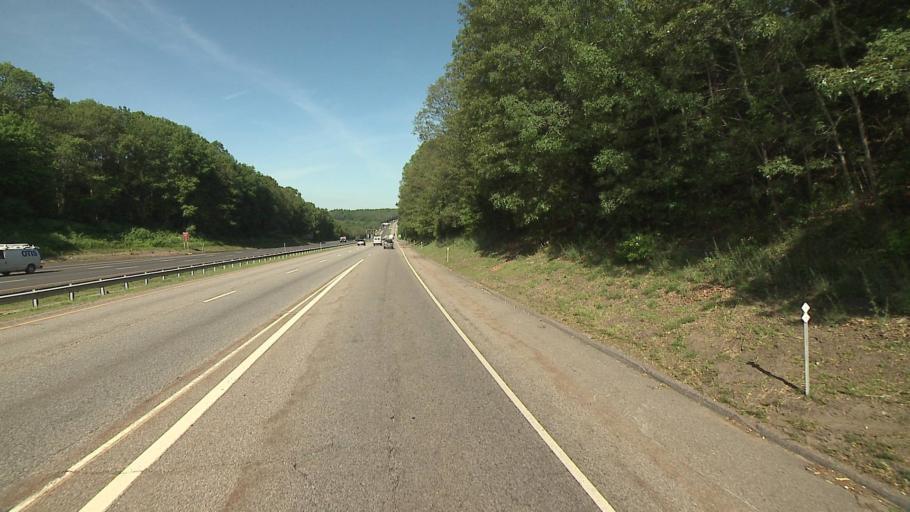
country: US
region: Connecticut
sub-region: New London County
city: Jewett City
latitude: 41.5905
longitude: -71.9793
